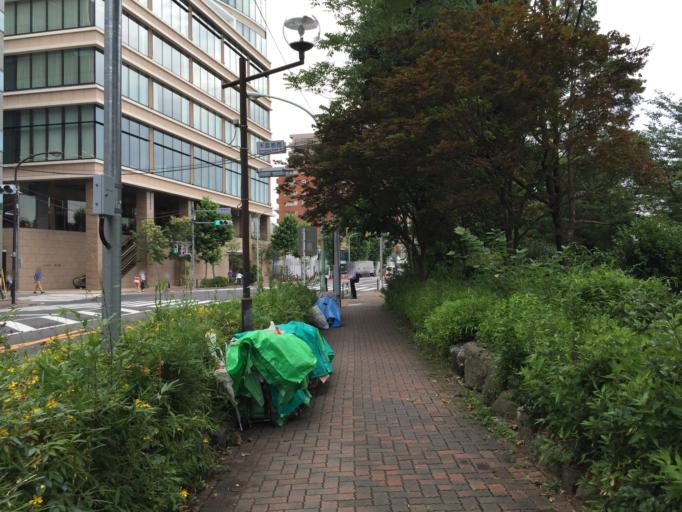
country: JP
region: Tokyo
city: Tokyo
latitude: 35.7101
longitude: 139.7689
